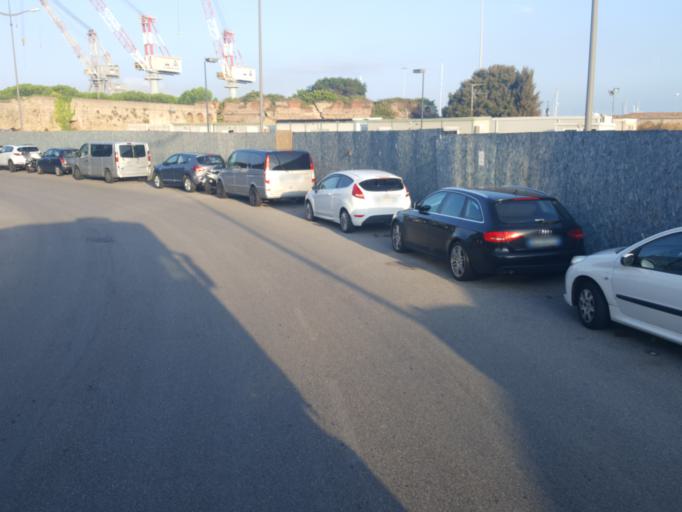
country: IT
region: Tuscany
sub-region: Provincia di Livorno
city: Livorno
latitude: 43.5452
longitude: 10.3008
